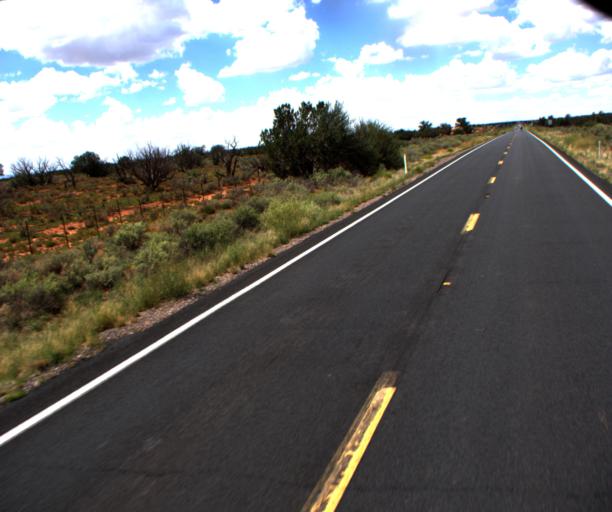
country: US
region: Arizona
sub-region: Coconino County
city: Williams
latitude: 35.6370
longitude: -112.1236
